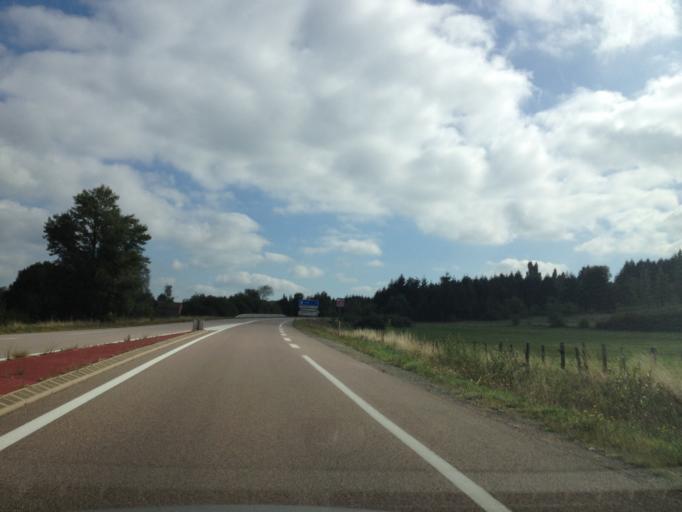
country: FR
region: Rhone-Alpes
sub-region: Departement de la Loire
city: Lentigny
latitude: 45.9627
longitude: 3.9789
